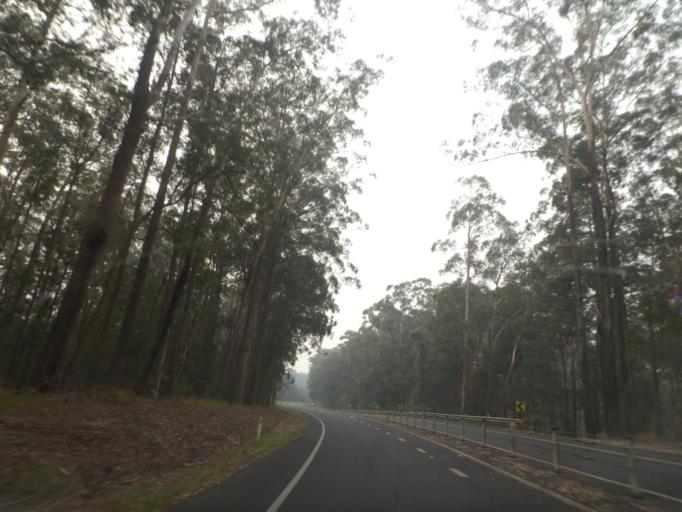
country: AU
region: New South Wales
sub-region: Coffs Harbour
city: Bonville
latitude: -30.4202
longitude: 153.0254
